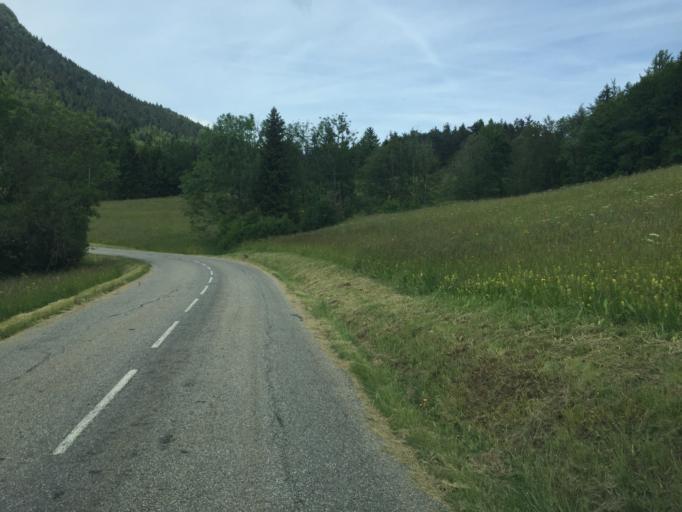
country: FR
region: Rhone-Alpes
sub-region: Departement de la Savoie
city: Saint-Baldoph
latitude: 45.4735
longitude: 5.9066
